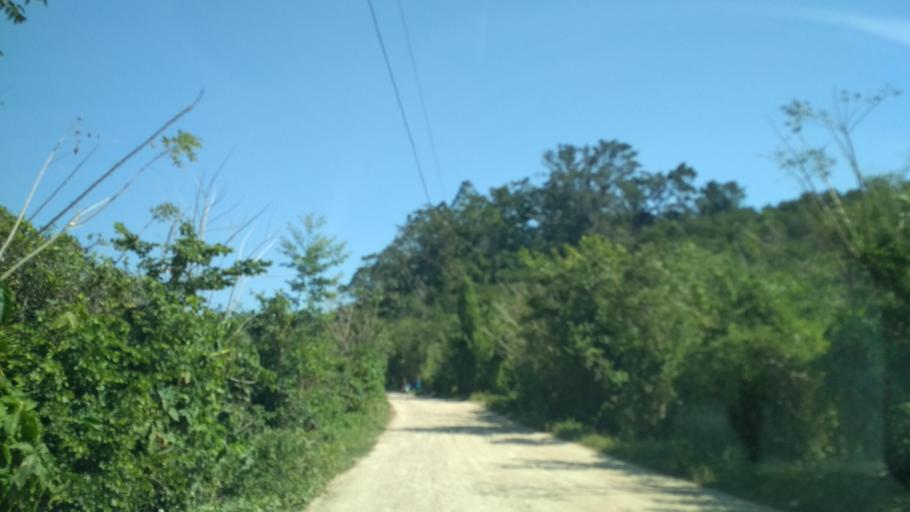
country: MX
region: Veracruz
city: Gutierrez Zamora
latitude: 20.4703
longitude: -97.1536
